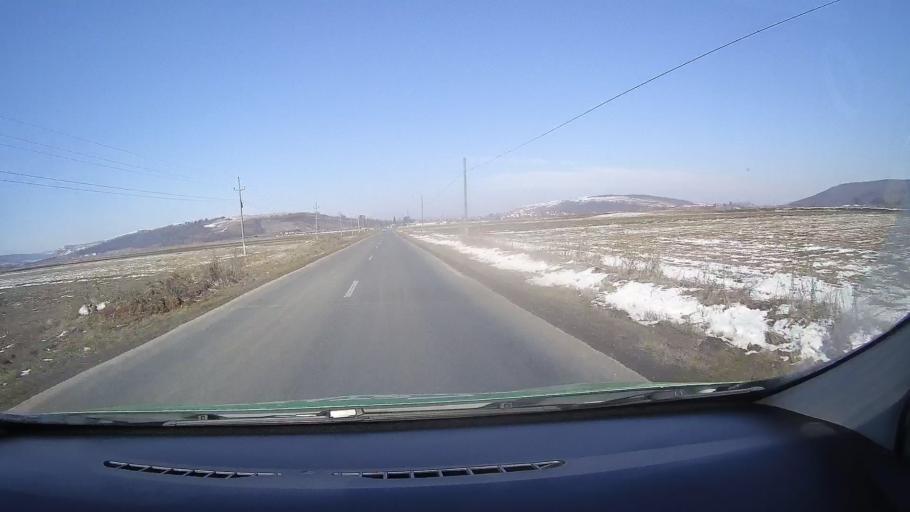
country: RO
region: Brasov
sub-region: Comuna Homorod
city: Homorod
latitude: 46.0265
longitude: 25.2740
